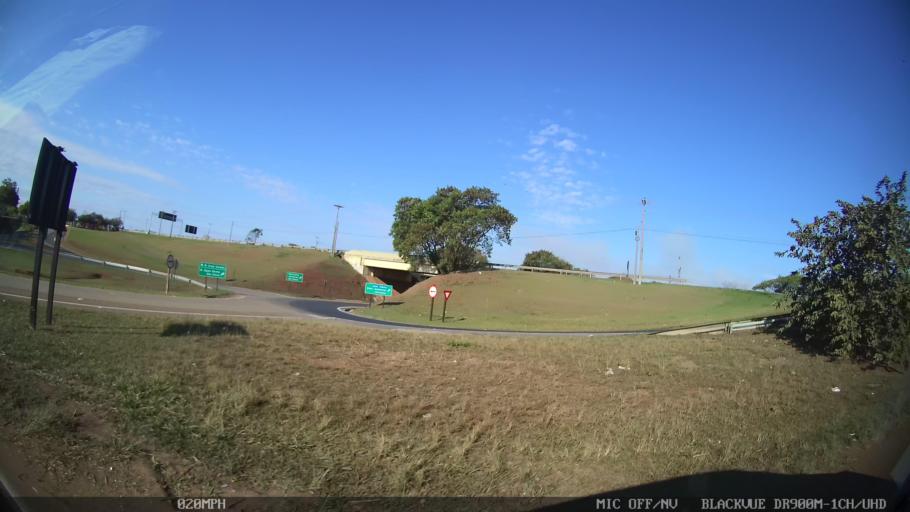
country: BR
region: Sao Paulo
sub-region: Piracicaba
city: Piracicaba
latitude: -22.6634
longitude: -47.6184
